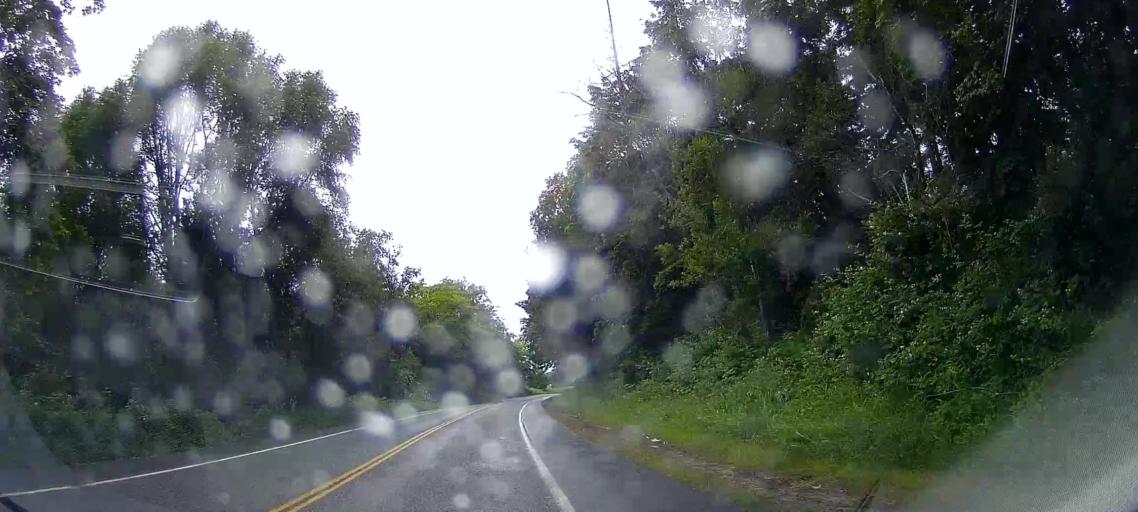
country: US
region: Washington
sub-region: Whatcom County
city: Birch Bay
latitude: 48.8562
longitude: -122.7011
